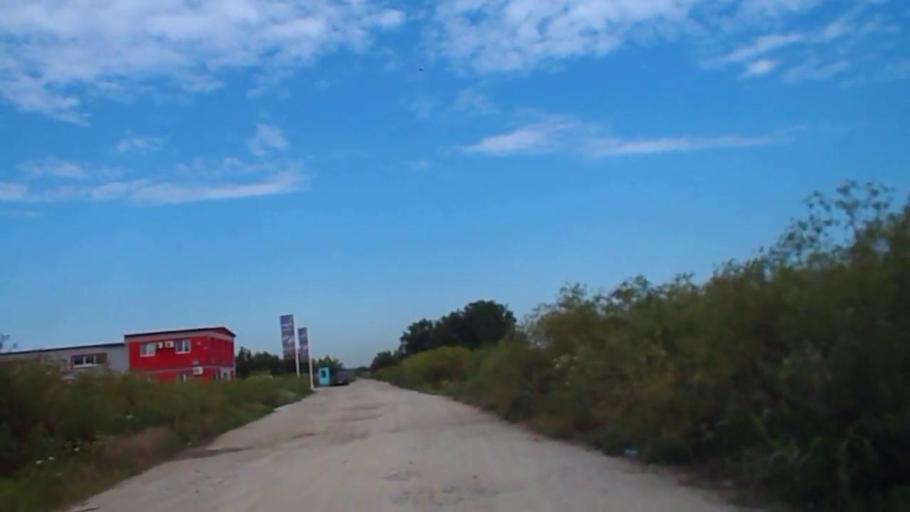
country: RO
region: Ilfov
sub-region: Comuna Jilava
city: Jilava
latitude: 44.3286
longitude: 26.0683
